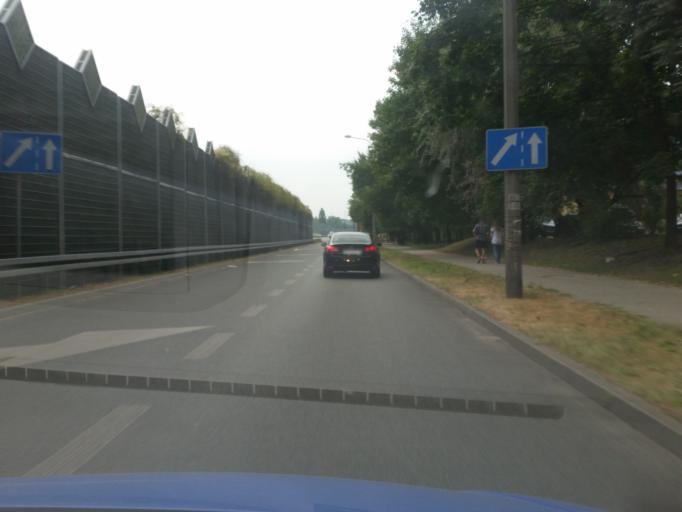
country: PL
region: Silesian Voivodeship
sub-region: Sosnowiec
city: Sosnowiec
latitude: 50.2903
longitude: 19.1121
